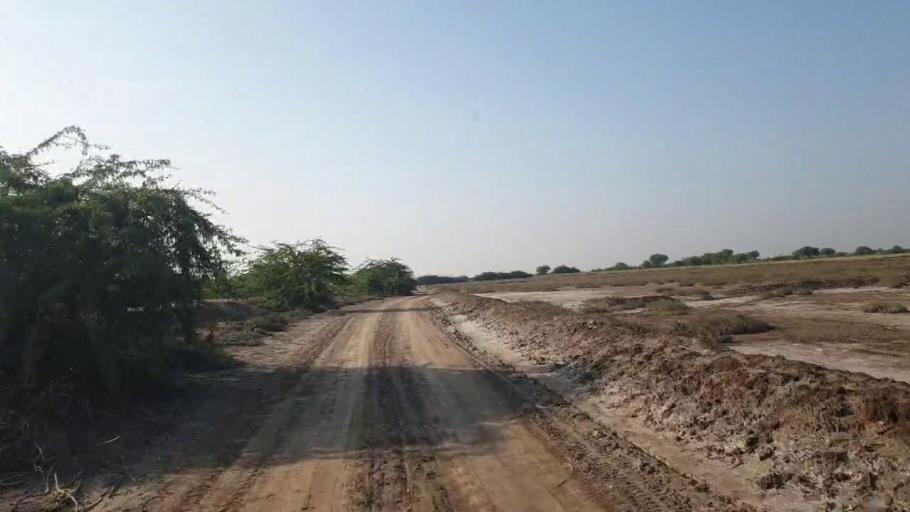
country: PK
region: Sindh
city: Badin
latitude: 24.4567
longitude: 68.7346
